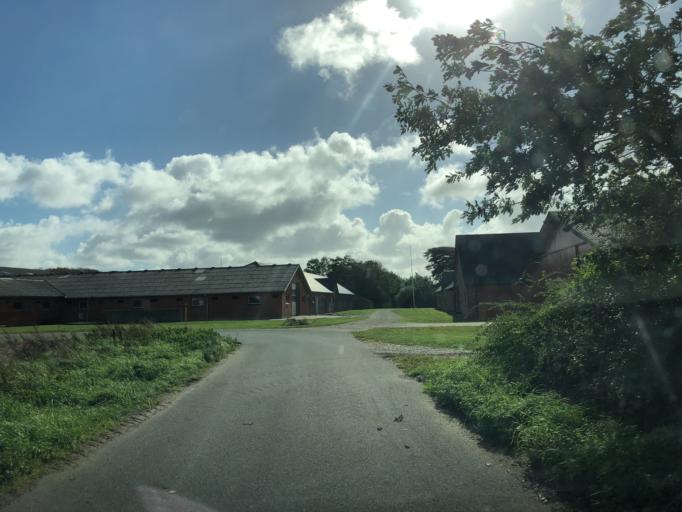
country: DK
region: Central Jutland
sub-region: Holstebro Kommune
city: Ulfborg
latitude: 56.2892
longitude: 8.3275
